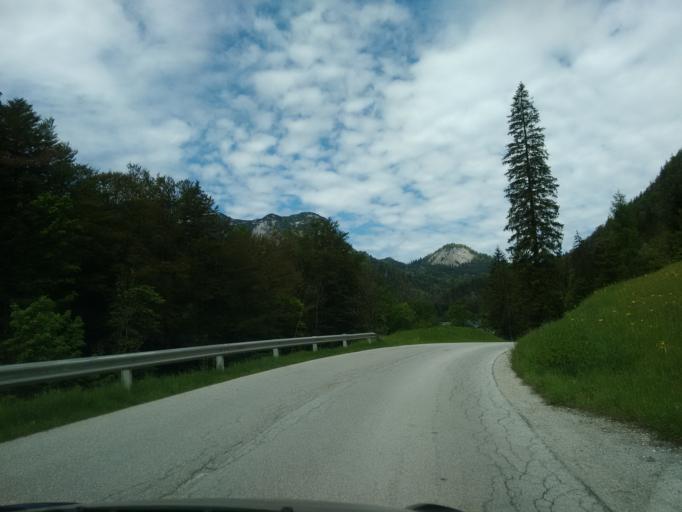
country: AT
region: Styria
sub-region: Politischer Bezirk Liezen
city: Altaussee
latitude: 47.6479
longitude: 13.7574
